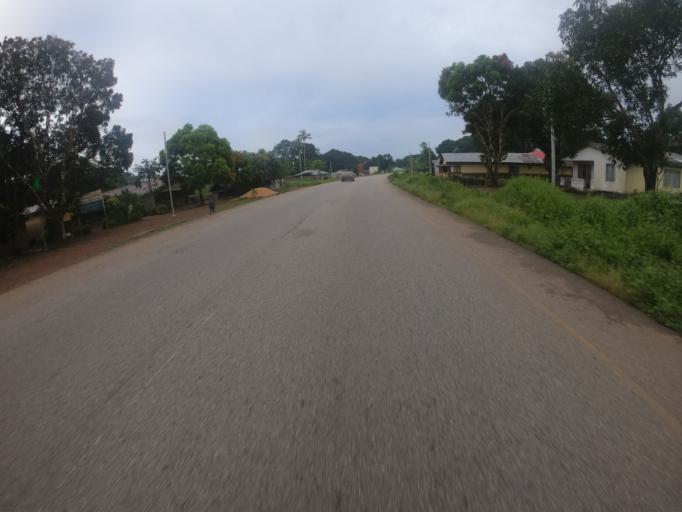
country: SL
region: Southern Province
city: Rotifunk
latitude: 8.4888
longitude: -12.7487
